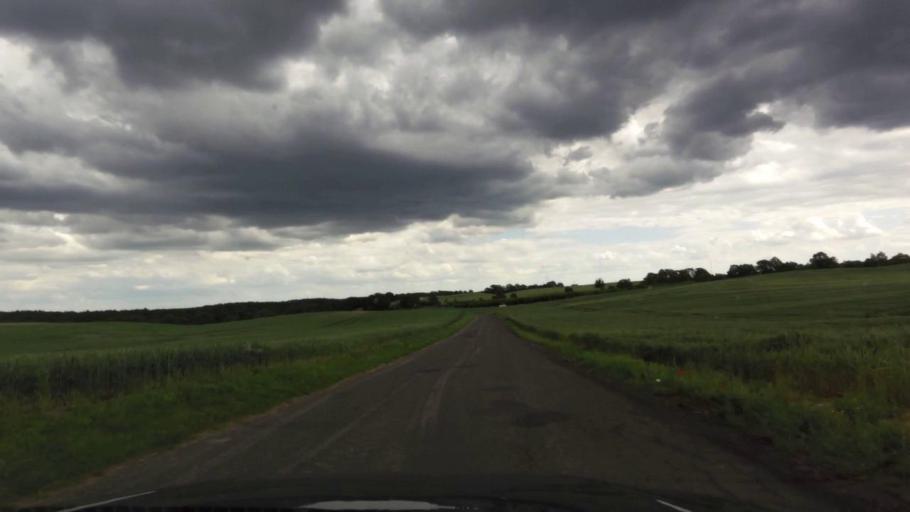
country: PL
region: West Pomeranian Voivodeship
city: Trzcinsko Zdroj
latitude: 52.9195
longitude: 14.5942
